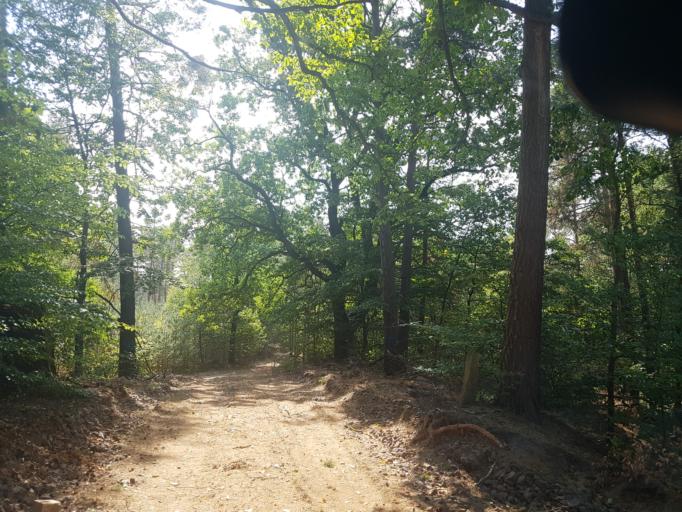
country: DE
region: Brandenburg
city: Gorzke
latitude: 52.0895
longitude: 12.3218
